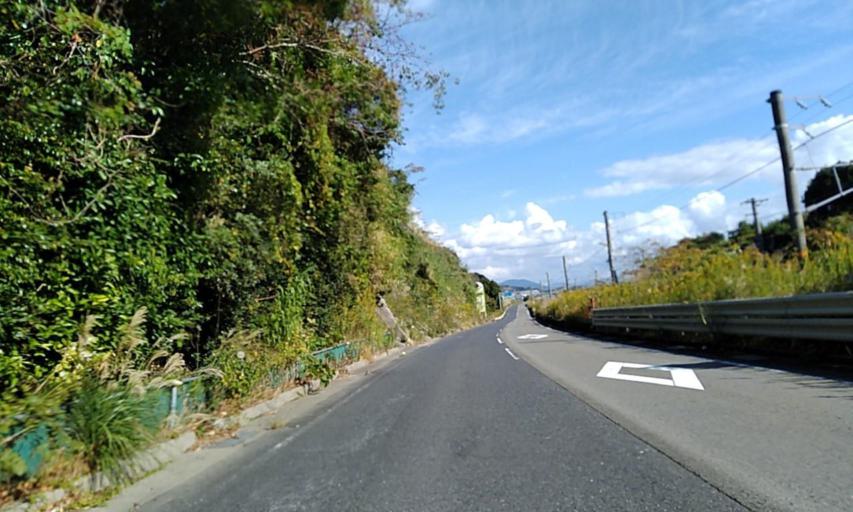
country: JP
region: Wakayama
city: Tanabe
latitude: 33.7835
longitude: 135.2549
